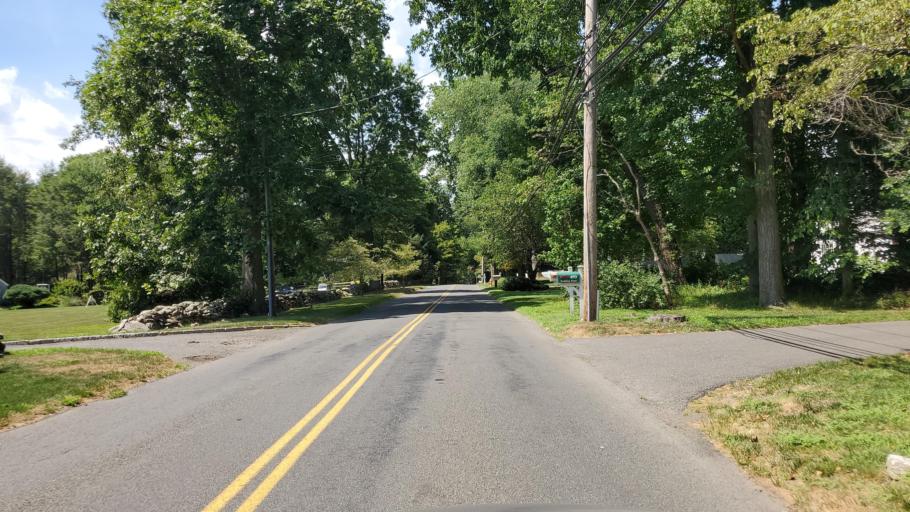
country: US
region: Connecticut
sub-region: Fairfield County
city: Southport
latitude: 41.1676
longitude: -73.2948
